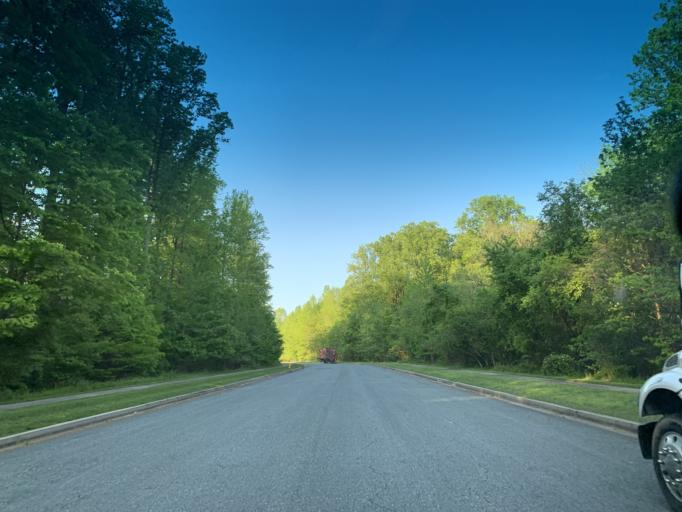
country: US
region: Maryland
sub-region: Harford County
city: Aberdeen
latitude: 39.5240
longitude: -76.1995
